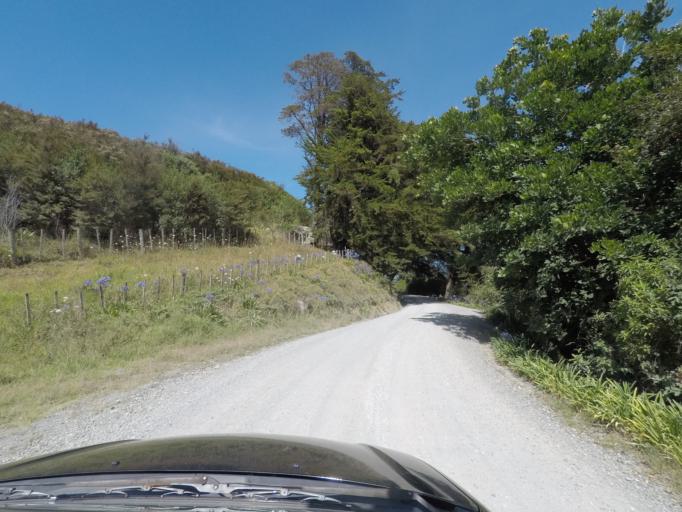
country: NZ
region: Auckland
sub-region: Auckland
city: Warkworth
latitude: -36.3166
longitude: 174.7863
